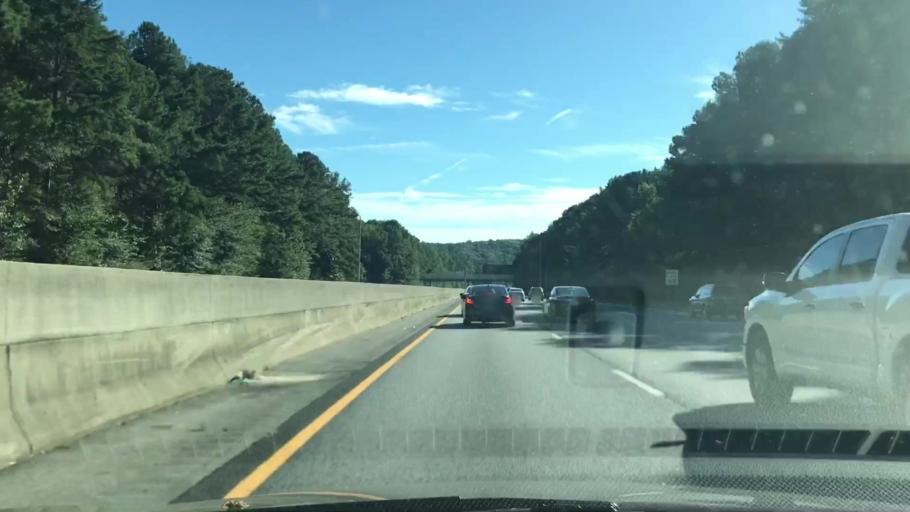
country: US
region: Georgia
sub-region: DeKalb County
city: Stone Mountain
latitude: 33.8213
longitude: -84.1634
